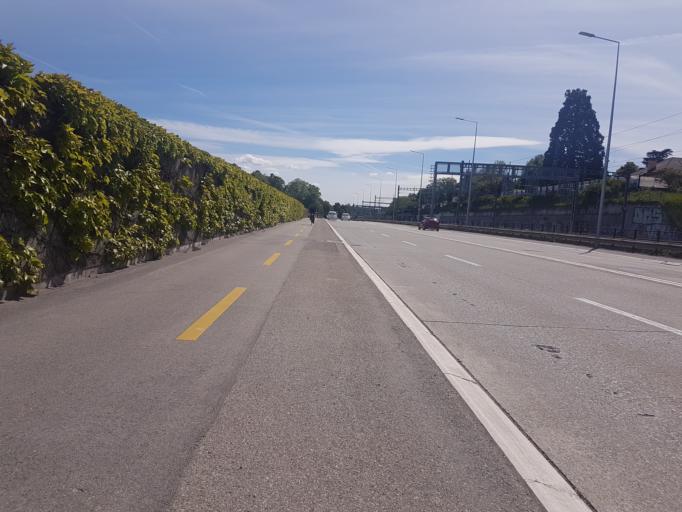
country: CH
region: Geneva
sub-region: Geneva
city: Bellevue
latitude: 46.2666
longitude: 6.1633
